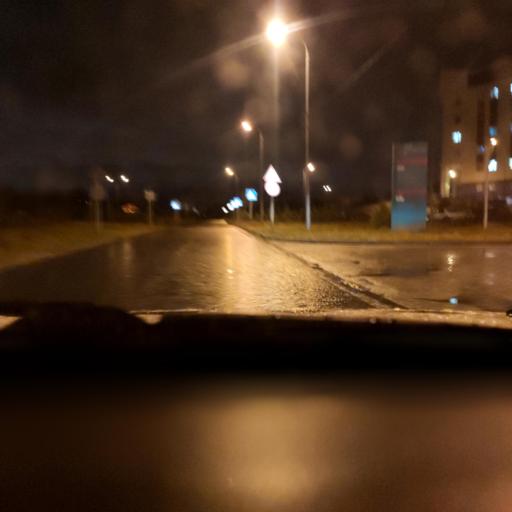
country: RU
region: Perm
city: Perm
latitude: 58.0350
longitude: 56.1773
